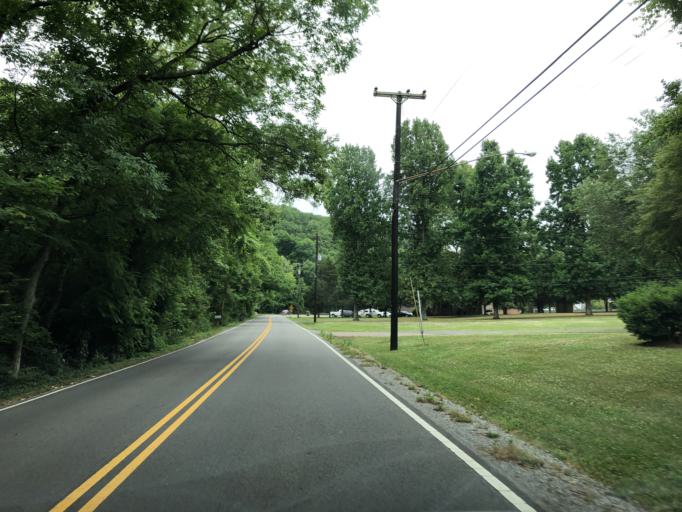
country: US
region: Tennessee
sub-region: Davidson County
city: Goodlettsville
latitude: 36.2898
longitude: -86.7800
